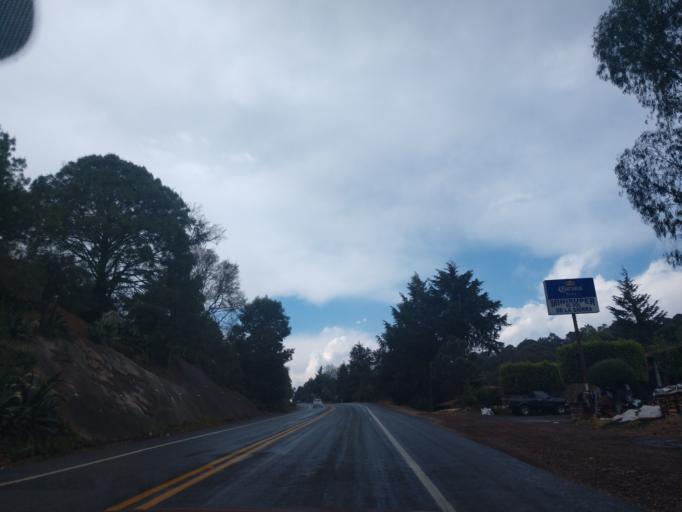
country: MX
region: Jalisco
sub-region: Mazamitla
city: Mazamitla
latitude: 19.9438
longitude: -103.0647
